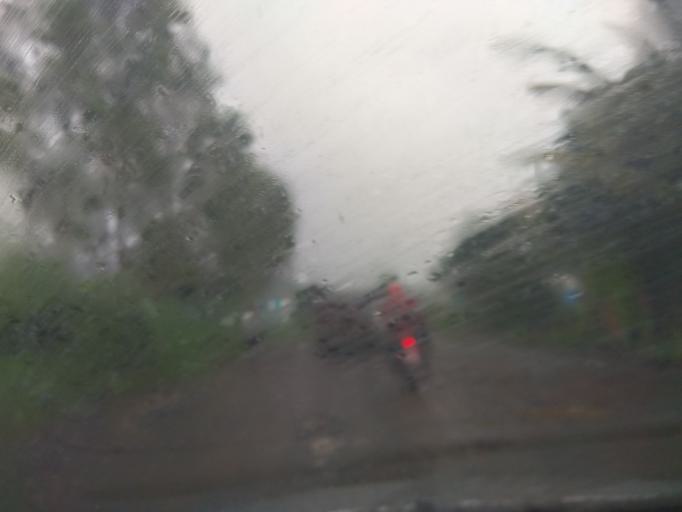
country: IN
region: Maharashtra
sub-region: Pune Division
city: Kharakvasla
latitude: 18.5146
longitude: 73.6612
